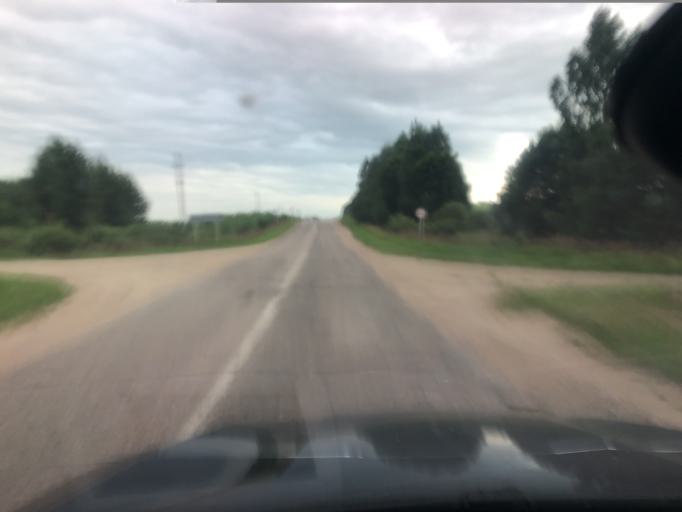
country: RU
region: Jaroslavl
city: Pereslavl'-Zalesskiy
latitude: 57.0233
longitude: 38.9398
